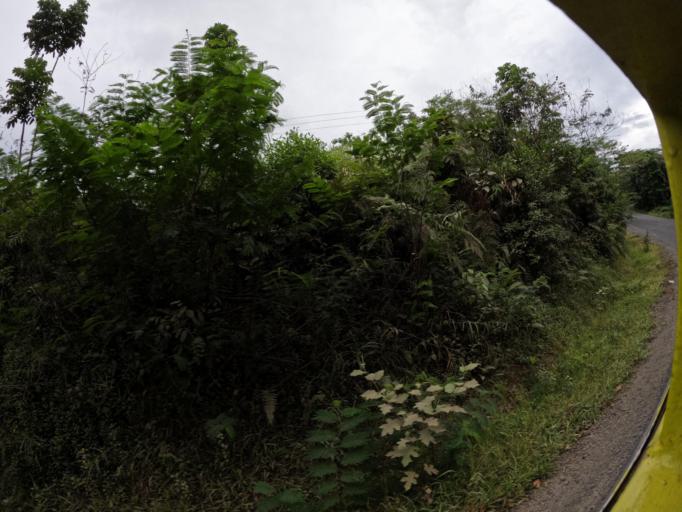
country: FJ
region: Central
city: Suva
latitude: -18.0642
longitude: 178.4585
